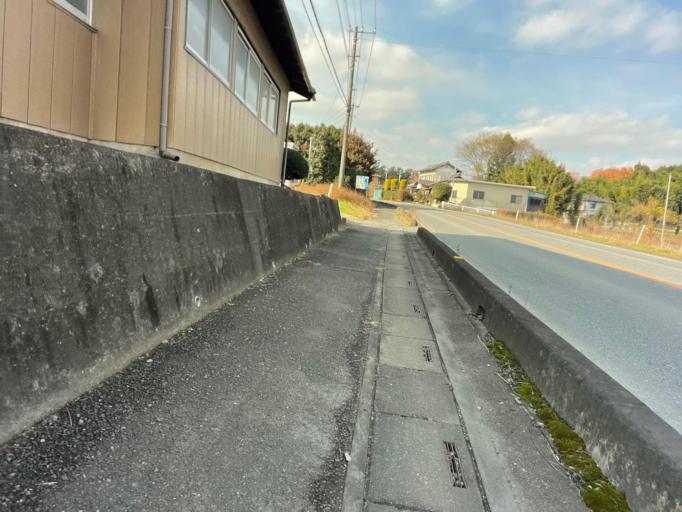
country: JP
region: Saitama
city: Yorii
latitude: 36.1565
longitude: 139.1907
